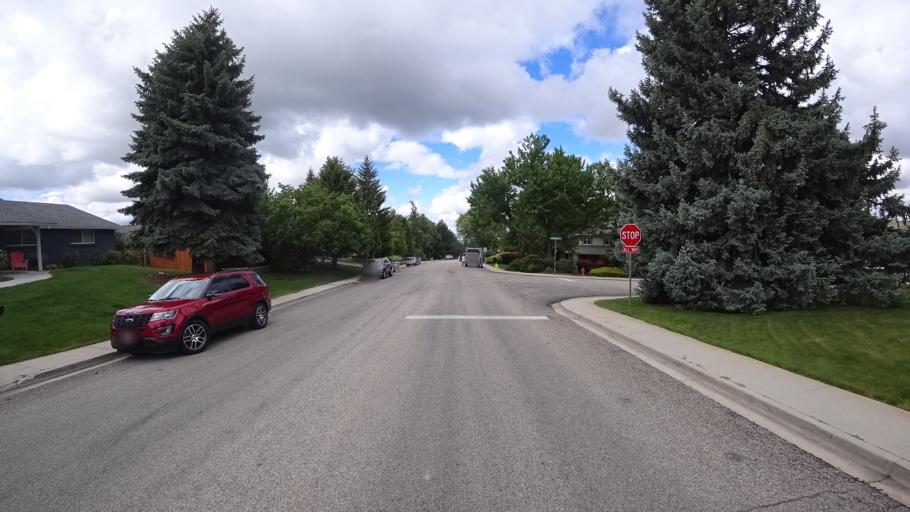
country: US
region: Idaho
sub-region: Ada County
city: Boise
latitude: 43.6501
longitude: -116.1851
